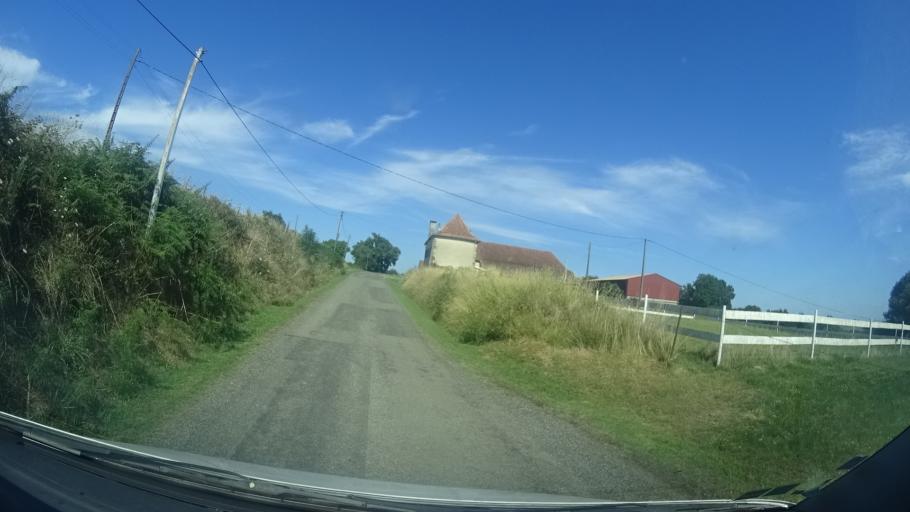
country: FR
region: Aquitaine
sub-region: Departement des Pyrenees-Atlantiques
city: Orthez
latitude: 43.5066
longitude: -0.7094
